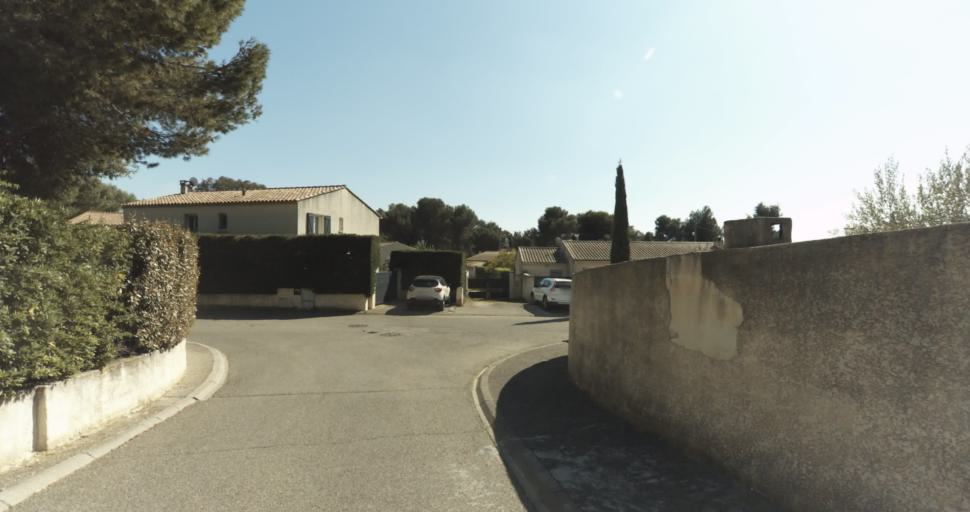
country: FR
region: Provence-Alpes-Cote d'Azur
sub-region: Departement des Bouches-du-Rhone
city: Pelissanne
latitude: 43.6386
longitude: 5.1579
